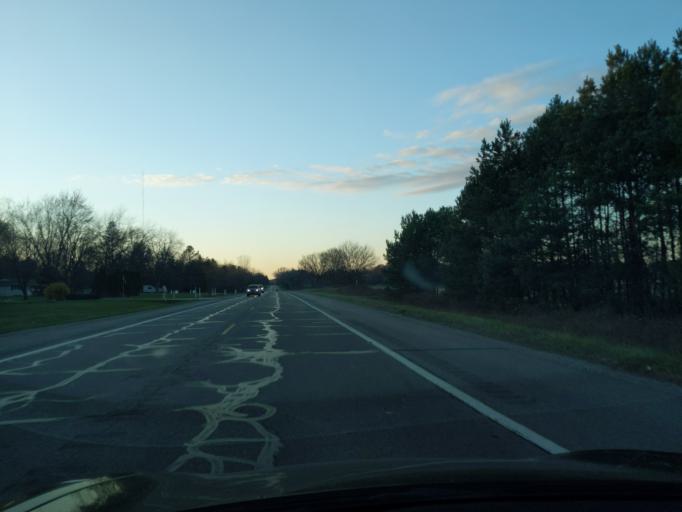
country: US
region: Michigan
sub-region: Ingham County
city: Williamston
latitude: 42.7040
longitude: -84.3471
